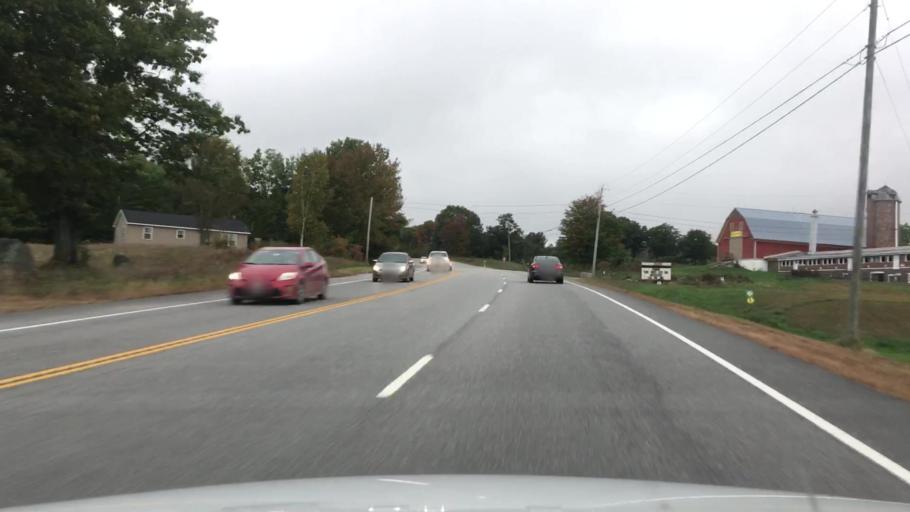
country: US
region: Maine
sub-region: Androscoggin County
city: Poland
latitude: 44.0834
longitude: -70.4186
